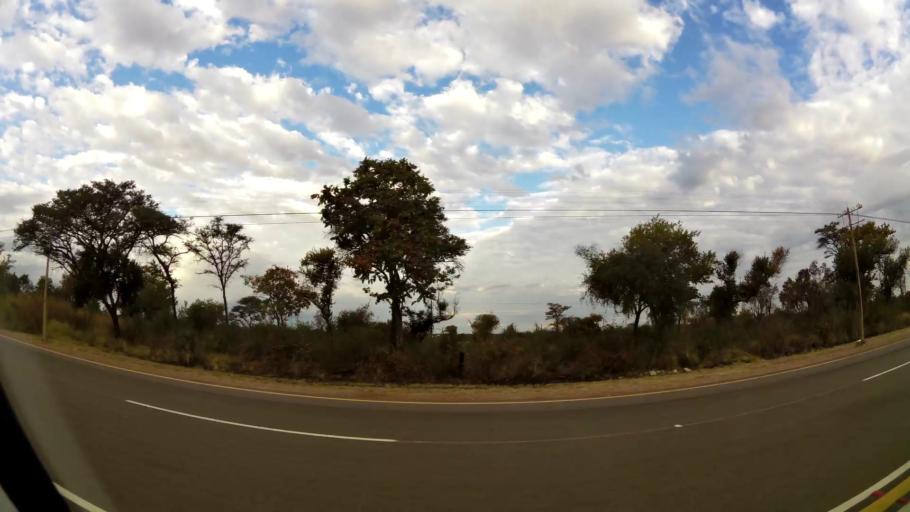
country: ZA
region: Limpopo
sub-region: Waterberg District Municipality
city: Modimolle
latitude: -24.5065
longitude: 28.7275
